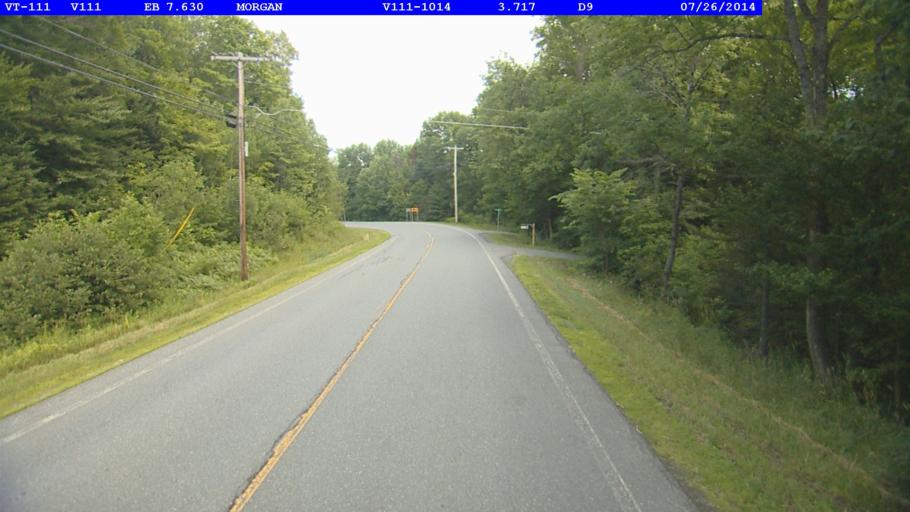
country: US
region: Vermont
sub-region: Orleans County
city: Newport
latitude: 44.9068
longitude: -71.9989
